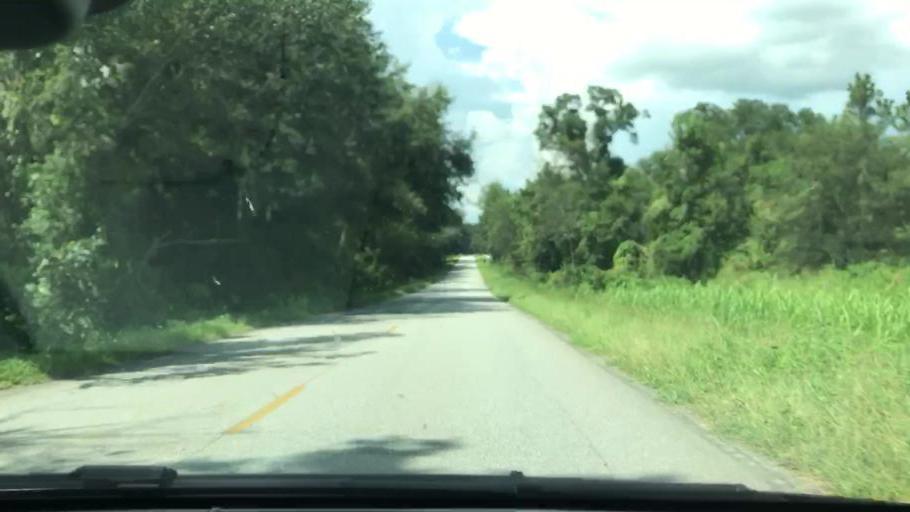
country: US
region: Georgia
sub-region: Seminole County
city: Donalsonville
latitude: 30.9864
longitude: -84.9772
